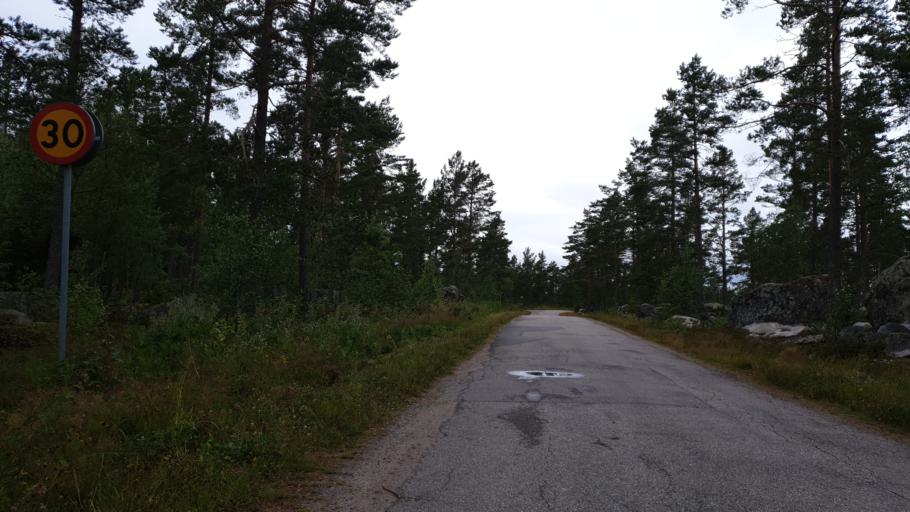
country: SE
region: Gaevleborg
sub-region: Soderhamns Kommun
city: Marielund
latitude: 61.4209
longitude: 17.1513
